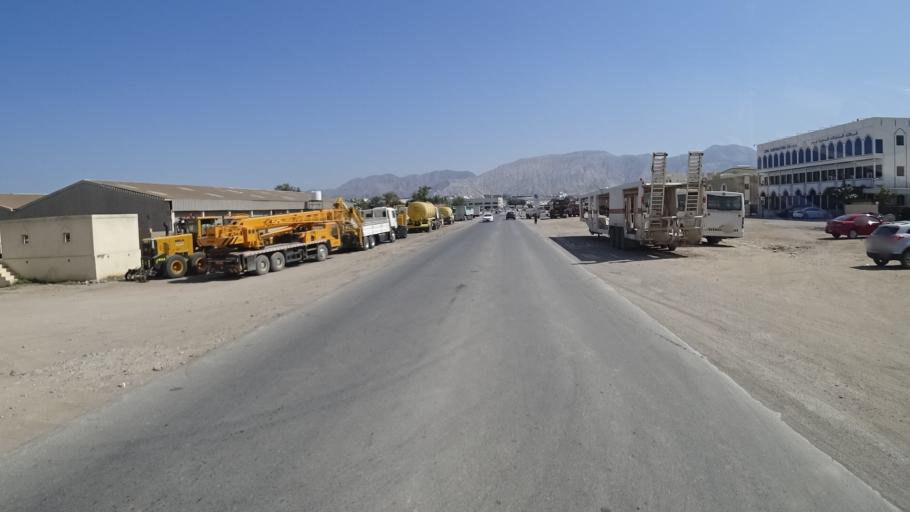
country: OM
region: Muhafazat Masqat
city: Bawshar
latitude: 23.5728
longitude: 58.3765
